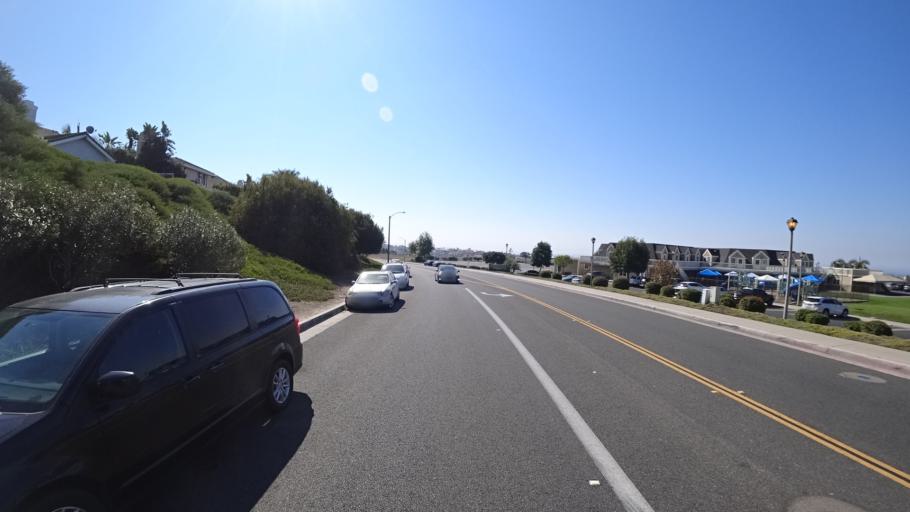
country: US
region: California
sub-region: Orange County
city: San Clemente
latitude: 33.4453
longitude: -117.6284
